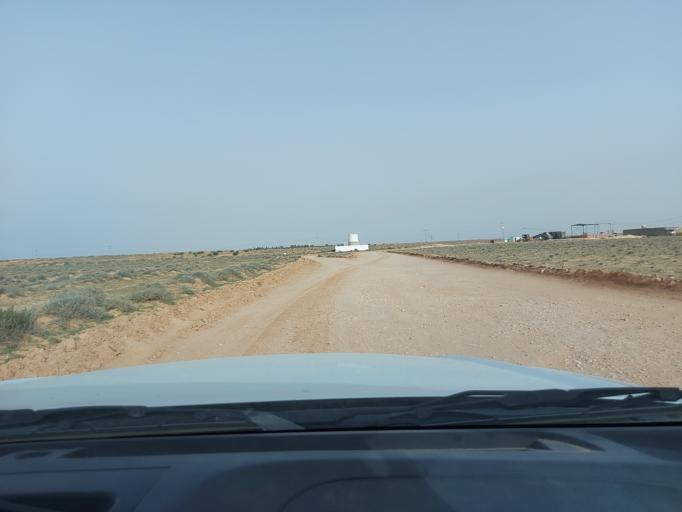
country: TN
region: Madanin
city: Medenine
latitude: 33.2649
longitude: 10.5706
